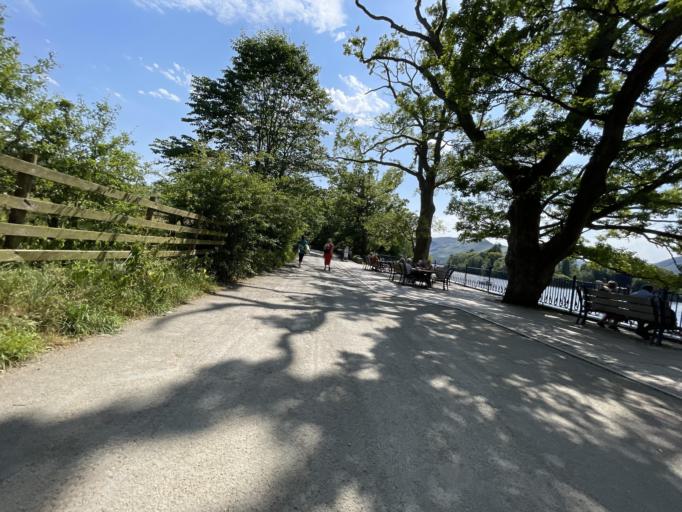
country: GB
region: England
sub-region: Cumbria
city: Keswick
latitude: 54.5940
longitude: -3.1403
